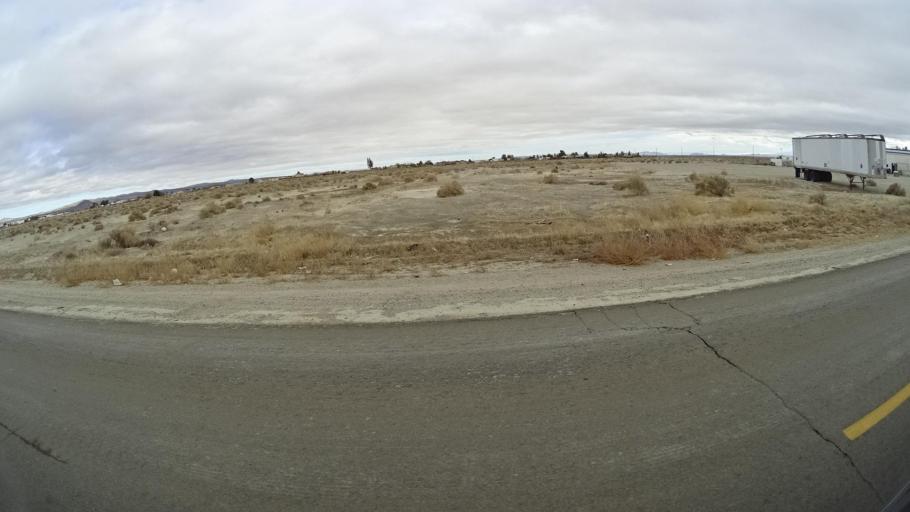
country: US
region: California
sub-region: Kern County
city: Rosamond
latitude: 34.8237
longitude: -118.1670
